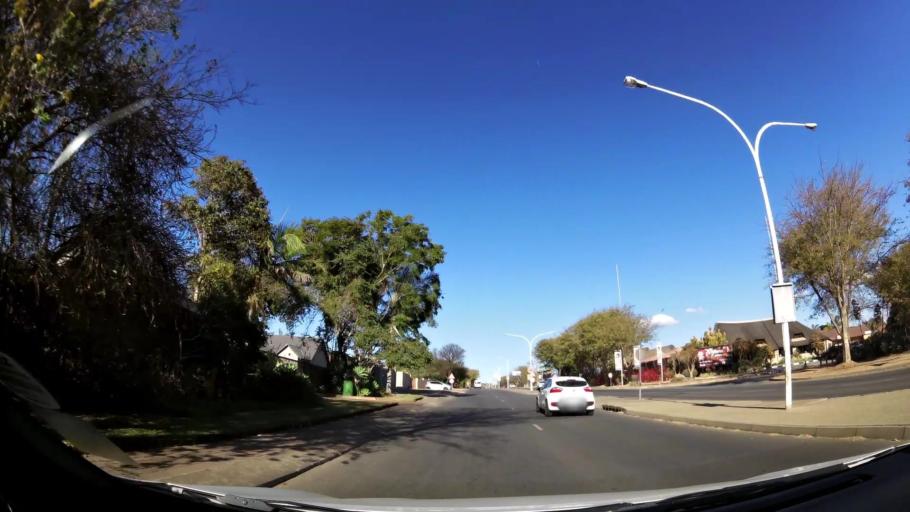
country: ZA
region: Limpopo
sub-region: Capricorn District Municipality
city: Polokwane
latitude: -23.8849
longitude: 29.4856
